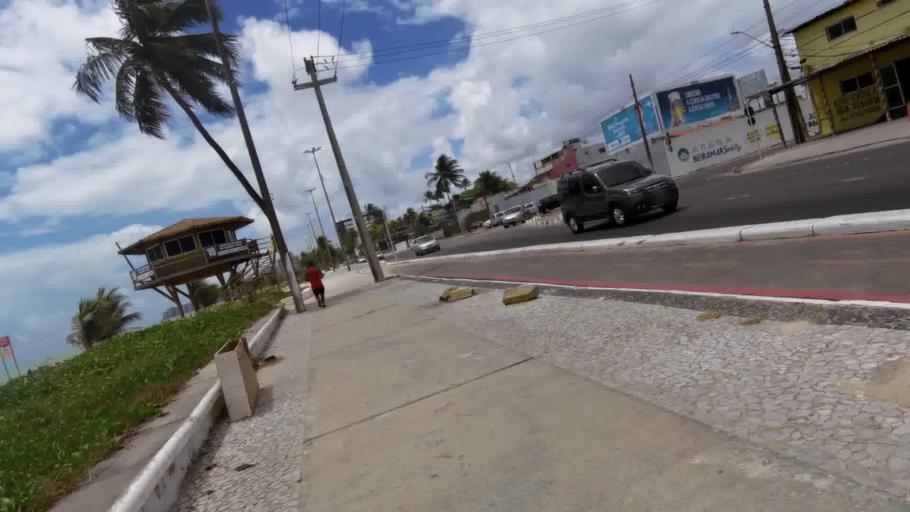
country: BR
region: Pernambuco
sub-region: Jaboatao Dos Guararapes
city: Jaboatao
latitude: -8.1593
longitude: -34.9111
